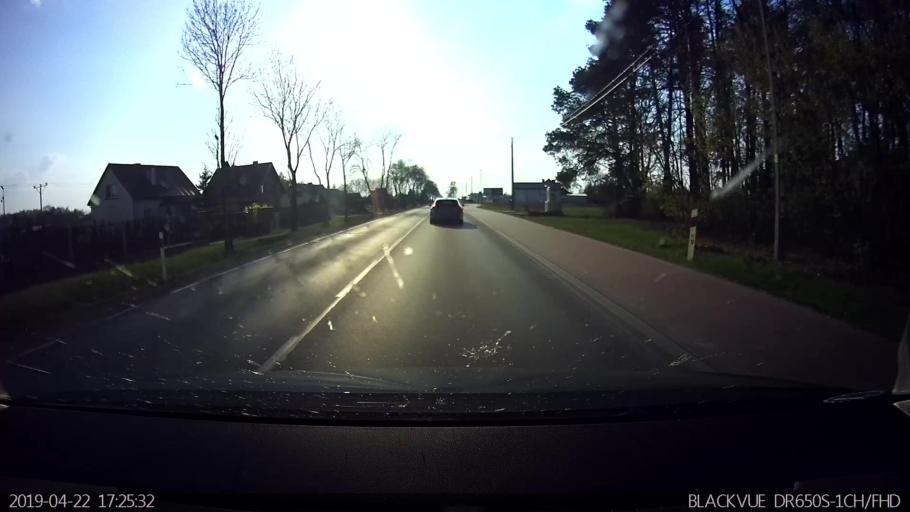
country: PL
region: Masovian Voivodeship
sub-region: Powiat sokolowski
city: Sokolow Podlaski
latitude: 52.3942
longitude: 22.2890
